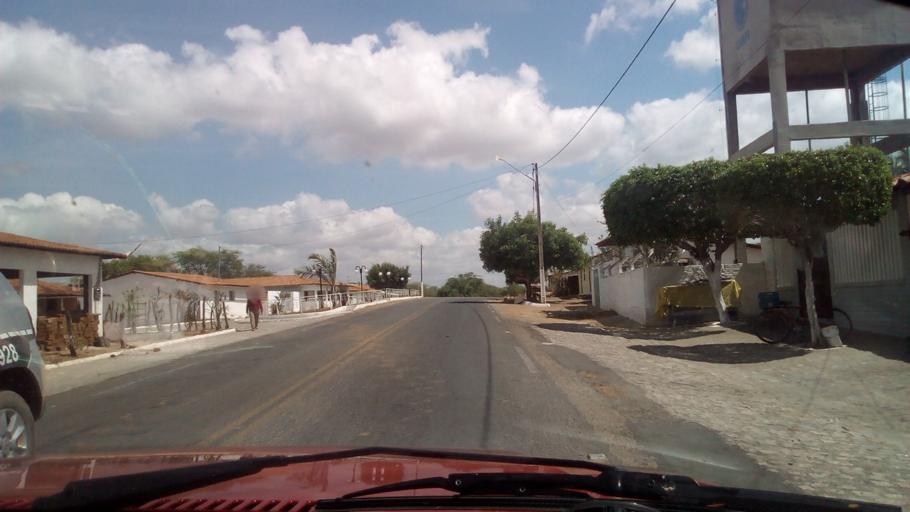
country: BR
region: Paraiba
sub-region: Dona Ines
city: Dona Ines
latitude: -6.5324
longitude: -35.6541
